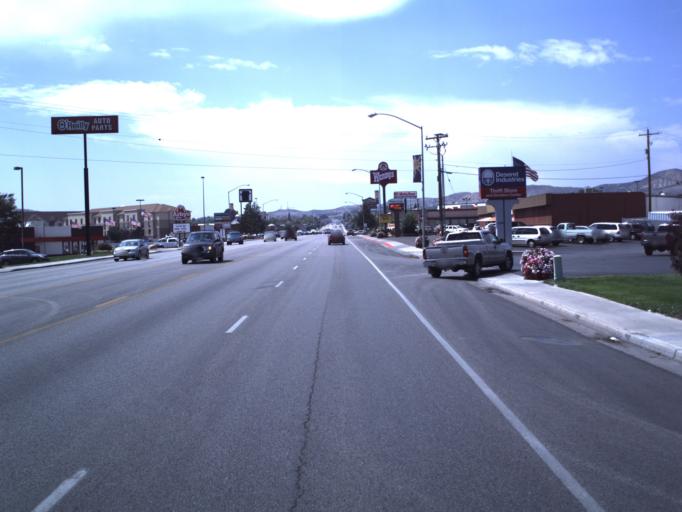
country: US
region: Utah
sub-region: Uintah County
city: Vernal
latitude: 40.4523
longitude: -109.5480
